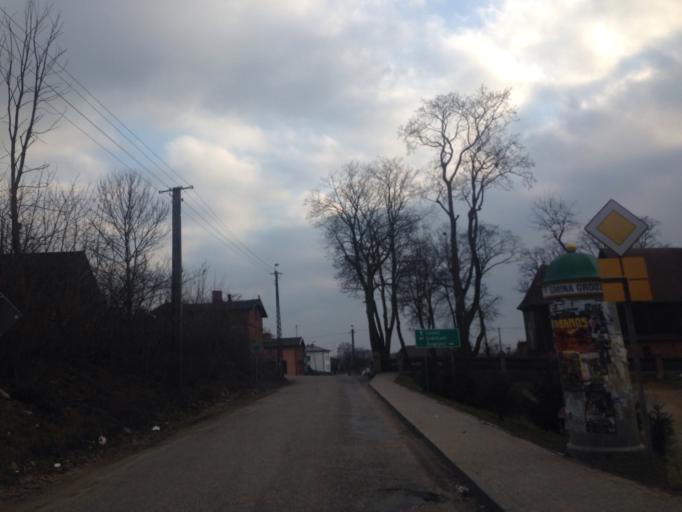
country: PL
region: Kujawsko-Pomorskie
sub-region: Powiat brodnicki
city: Brzozie
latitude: 53.3242
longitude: 19.7178
